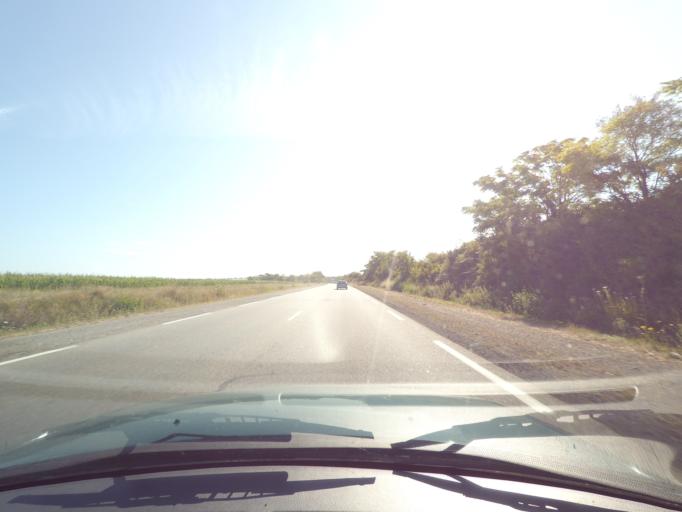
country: FR
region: Poitou-Charentes
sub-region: Departement de la Vienne
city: Migne-Auxances
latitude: 46.6307
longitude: 0.2720
